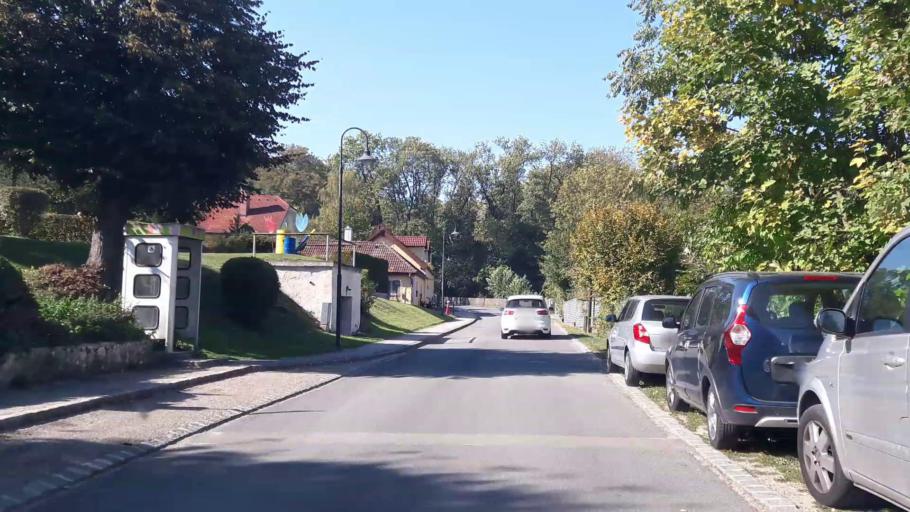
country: AT
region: Lower Austria
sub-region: Politischer Bezirk Korneuburg
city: Ernstbrunn
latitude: 48.5424
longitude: 16.3505
